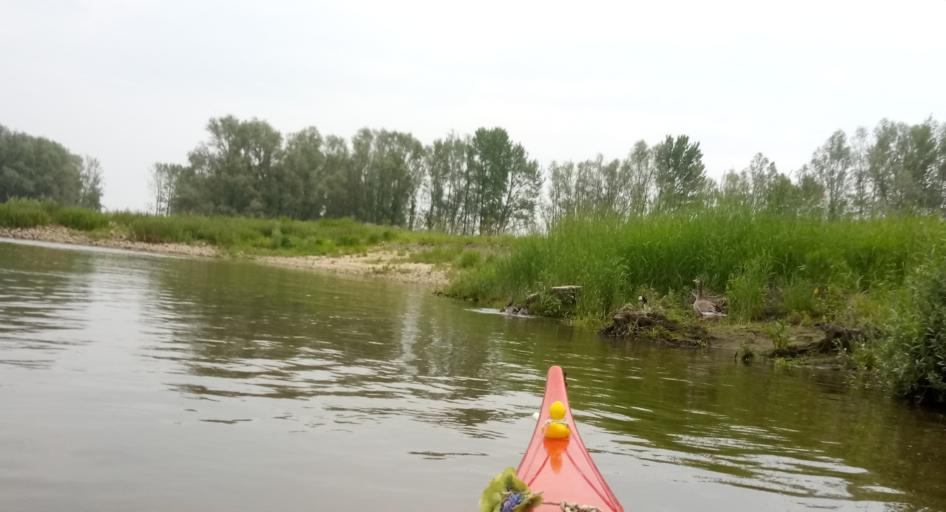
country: NL
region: Gelderland
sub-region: Gemeente Lochem
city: Gorssel
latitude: 52.1811
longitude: 6.1804
